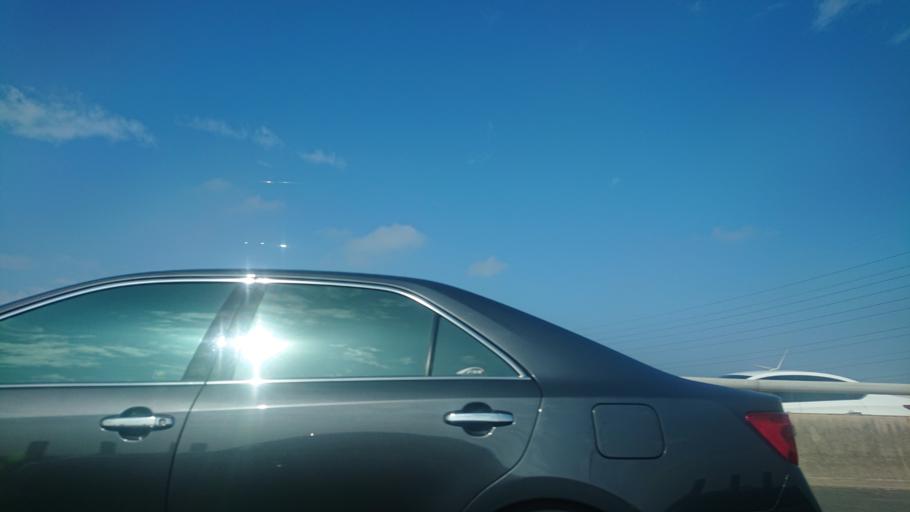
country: TW
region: Taiwan
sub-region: Changhua
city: Chang-hua
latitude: 24.0799
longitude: 120.4183
